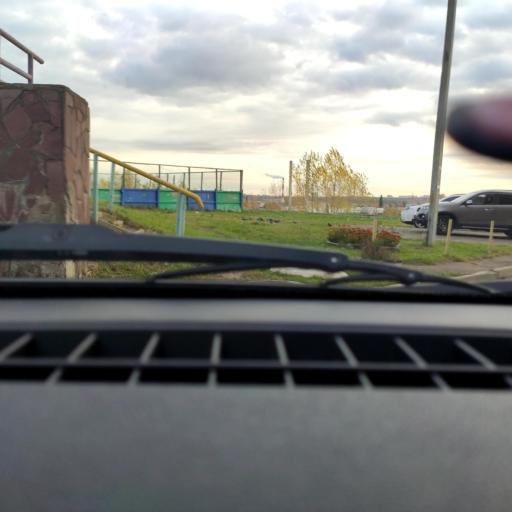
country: RU
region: Bashkortostan
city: Ufa
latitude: 54.7771
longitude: 56.0466
